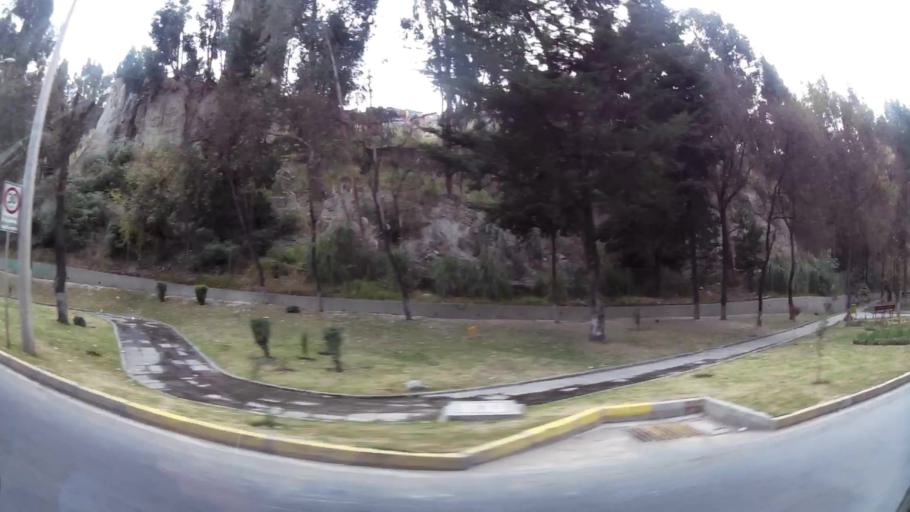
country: BO
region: La Paz
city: La Paz
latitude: -16.5077
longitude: -68.1231
